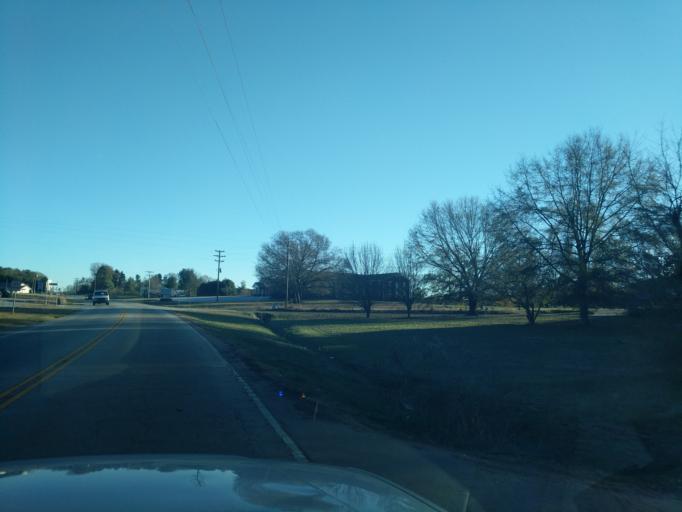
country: US
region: South Carolina
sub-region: Oconee County
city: Westminster
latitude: 34.6294
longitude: -83.0578
